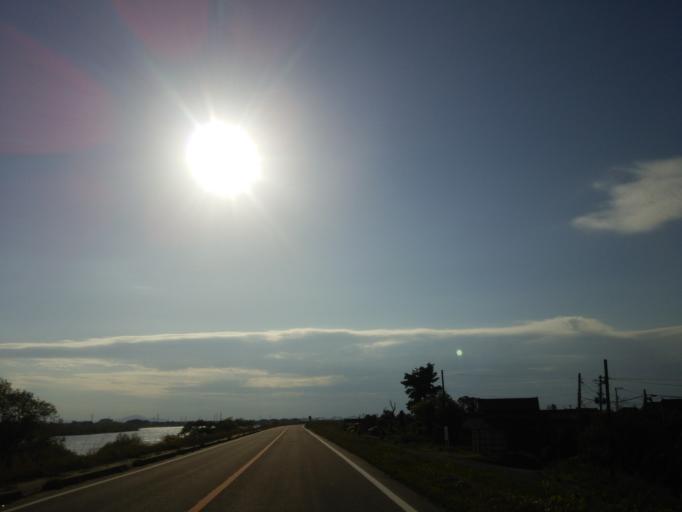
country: JP
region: Niigata
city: Niitsu-honcho
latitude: 37.8072
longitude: 139.1762
